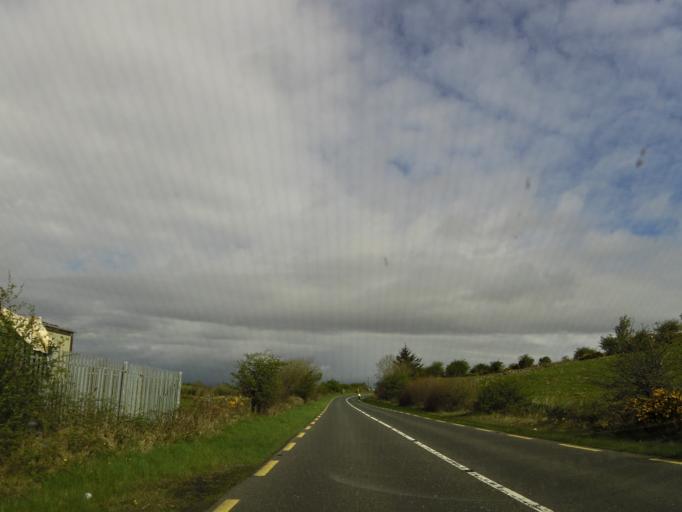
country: IE
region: Connaught
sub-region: Sligo
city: Tobercurry
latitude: 53.9461
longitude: -8.7924
